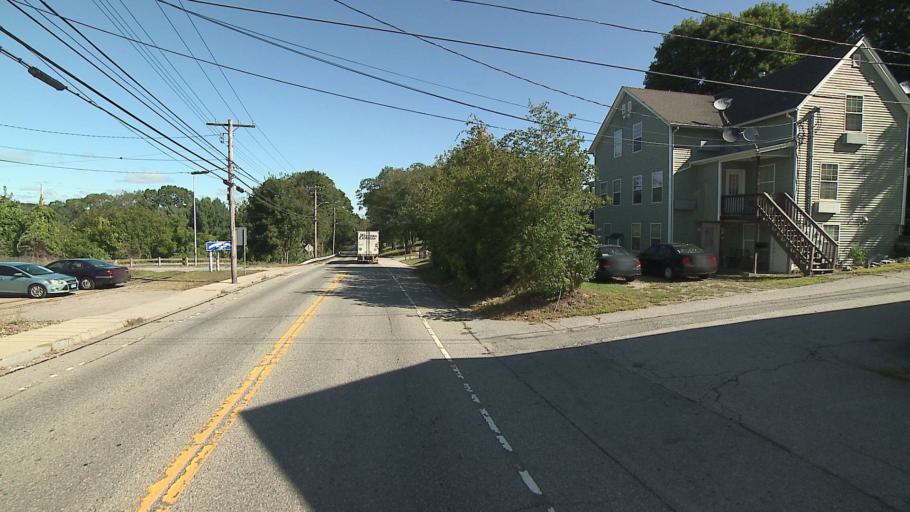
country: US
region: Connecticut
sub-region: New London County
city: Jewett City
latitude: 41.6143
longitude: -71.9792
